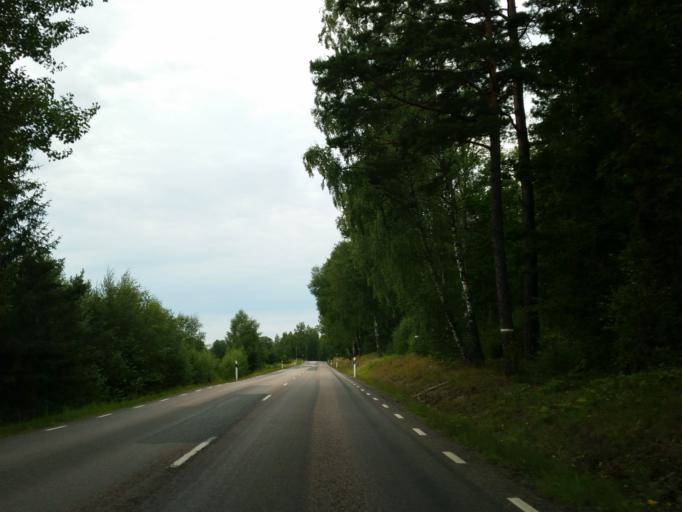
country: SE
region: Stockholm
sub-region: Nykvarns Kommun
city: Nykvarn
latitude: 59.1890
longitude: 17.4886
